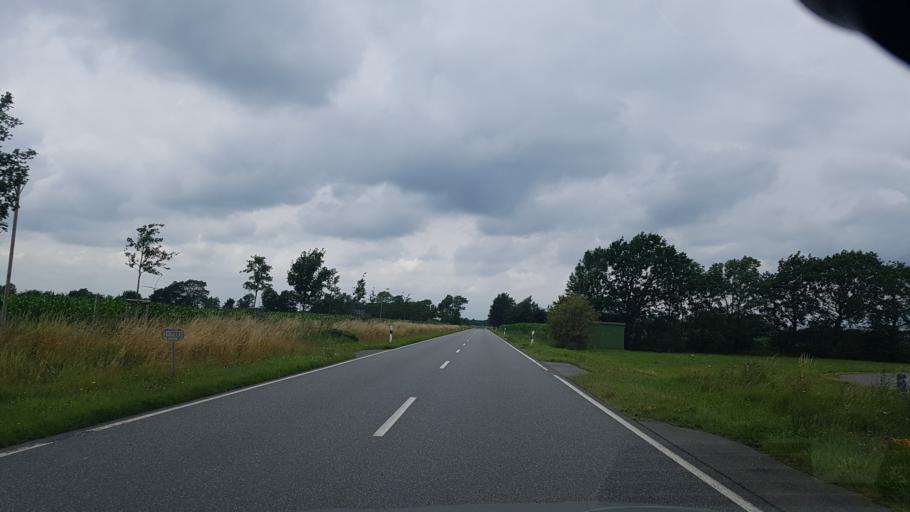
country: DE
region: Schleswig-Holstein
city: Boxlund
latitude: 54.8497
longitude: 9.1946
